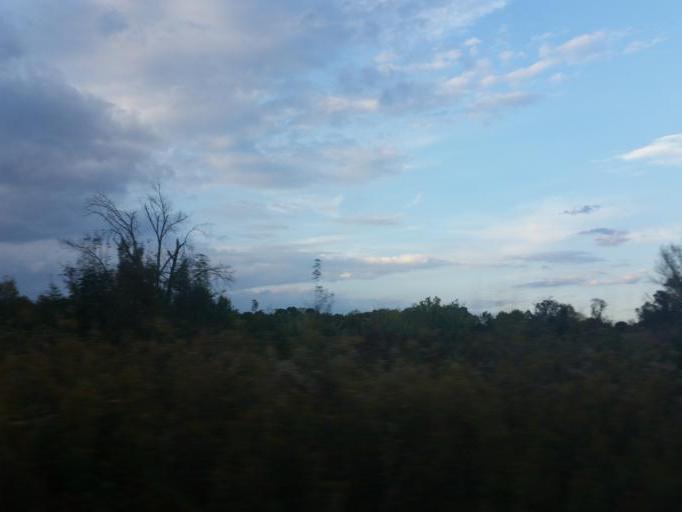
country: US
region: Tennessee
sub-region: Blount County
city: Louisville
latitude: 35.7684
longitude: -84.0412
